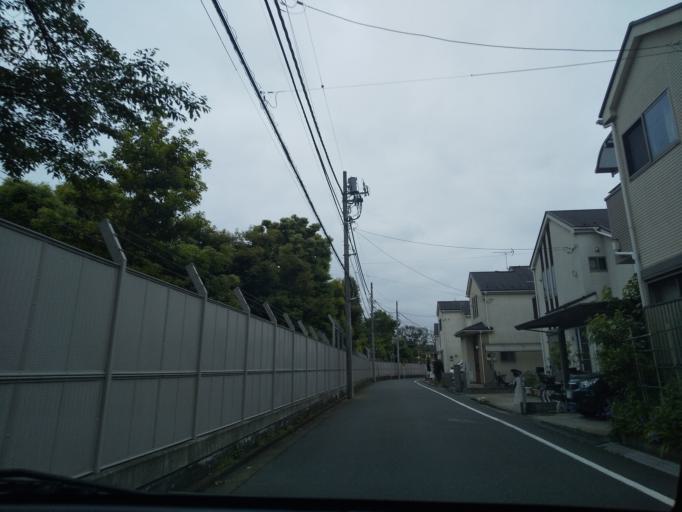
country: JP
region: Tokyo
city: Hino
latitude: 35.6534
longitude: 139.3653
